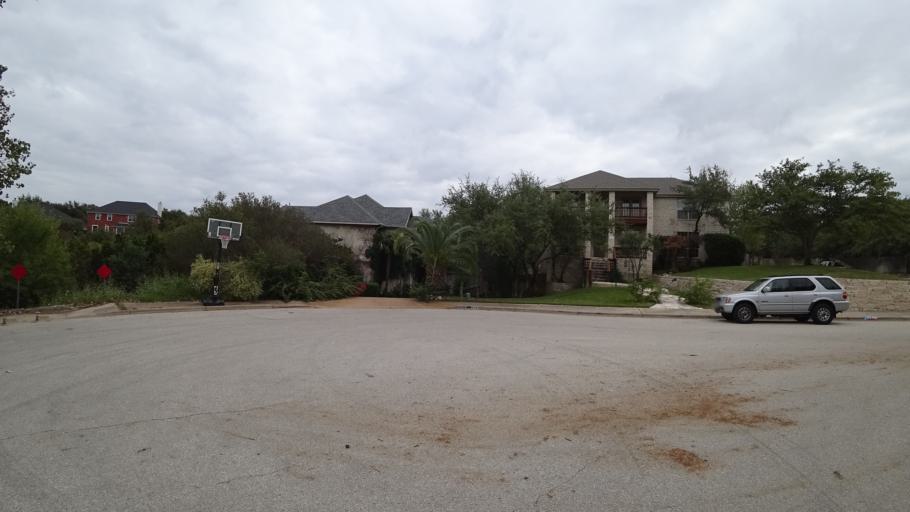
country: US
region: Texas
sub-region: Travis County
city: Bee Cave
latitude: 30.3126
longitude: -97.9325
